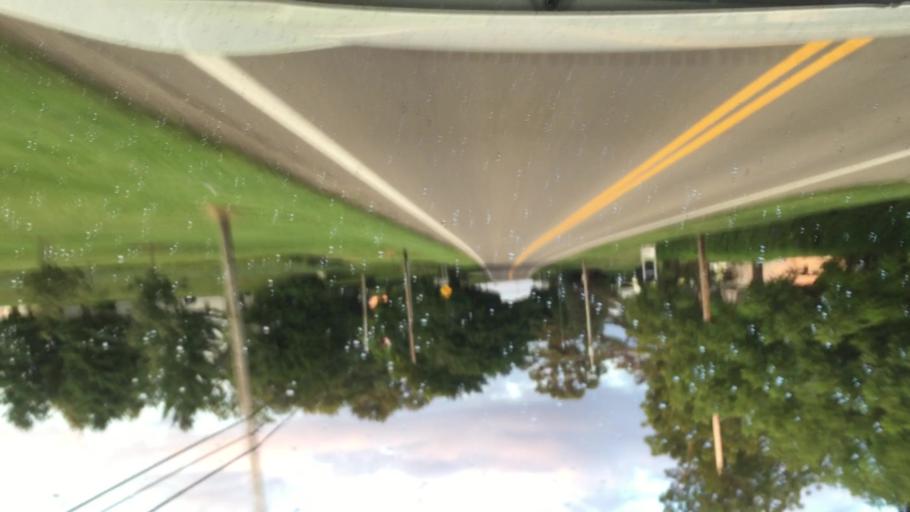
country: US
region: Ohio
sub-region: Champaign County
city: Mechanicsburg
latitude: 40.0676
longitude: -83.5510
